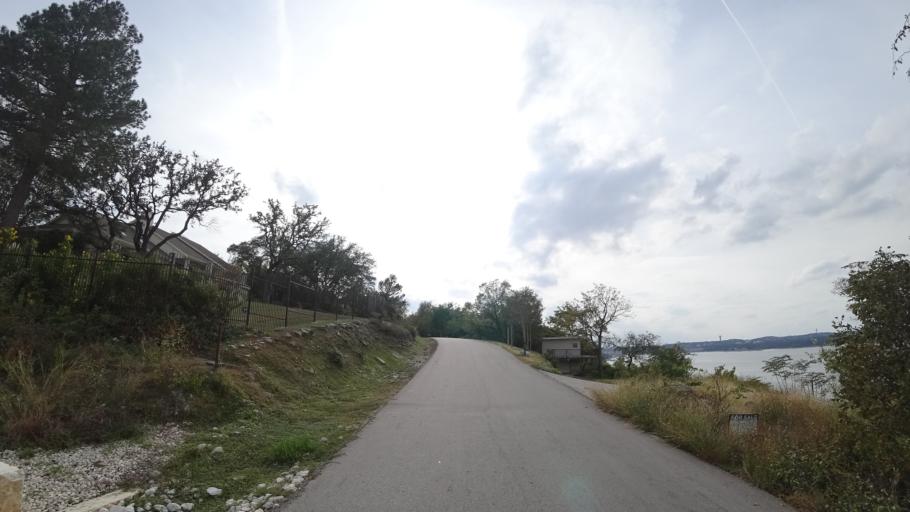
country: US
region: Texas
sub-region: Travis County
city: Hudson Bend
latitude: 30.3953
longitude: -97.8837
